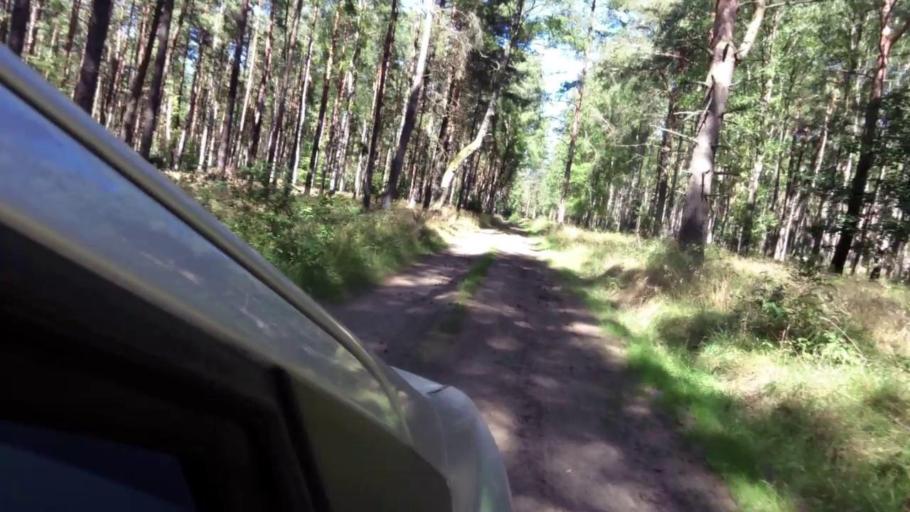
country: PL
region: West Pomeranian Voivodeship
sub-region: Powiat szczecinecki
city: Bialy Bor
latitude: 53.8199
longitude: 16.8631
